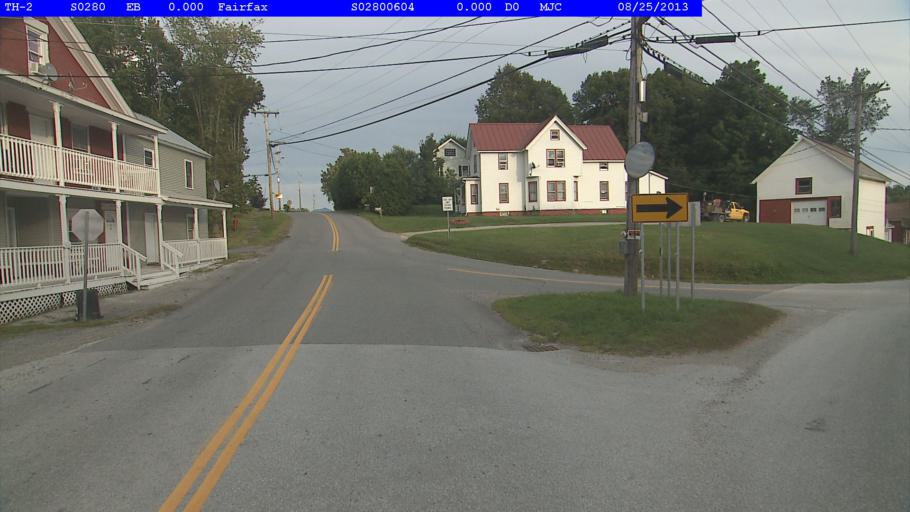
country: US
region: Vermont
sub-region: Chittenden County
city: Milton
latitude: 44.6652
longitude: -73.0088
